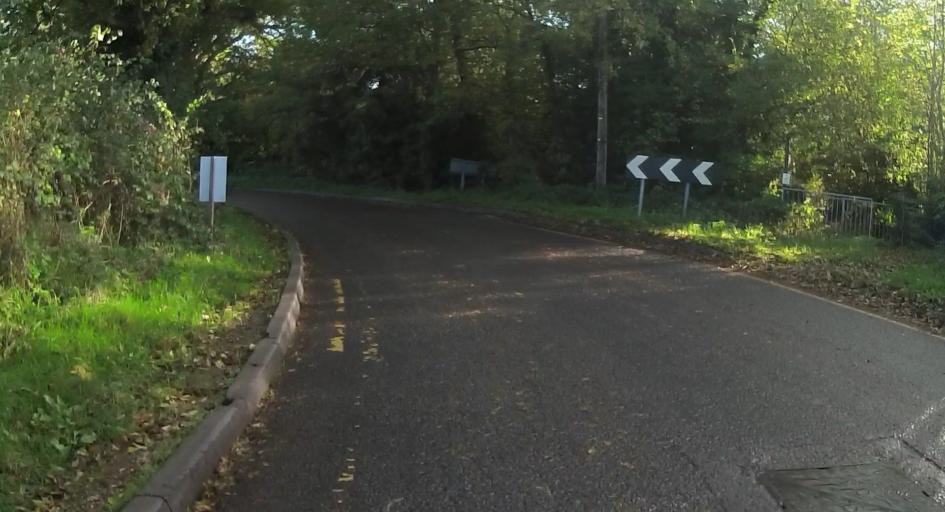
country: GB
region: England
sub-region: Wokingham
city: Wokingham
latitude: 51.4207
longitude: -0.8331
